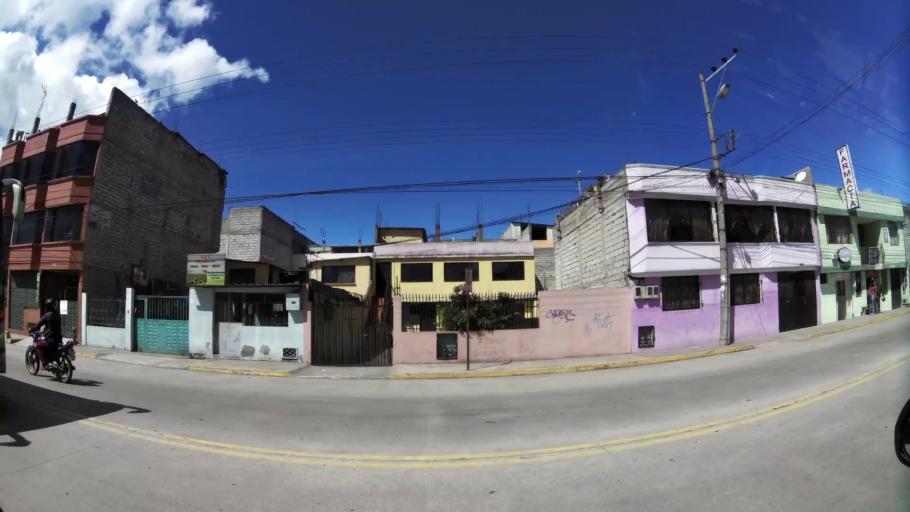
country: EC
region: Pichincha
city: Quito
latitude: -0.3033
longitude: -78.5488
